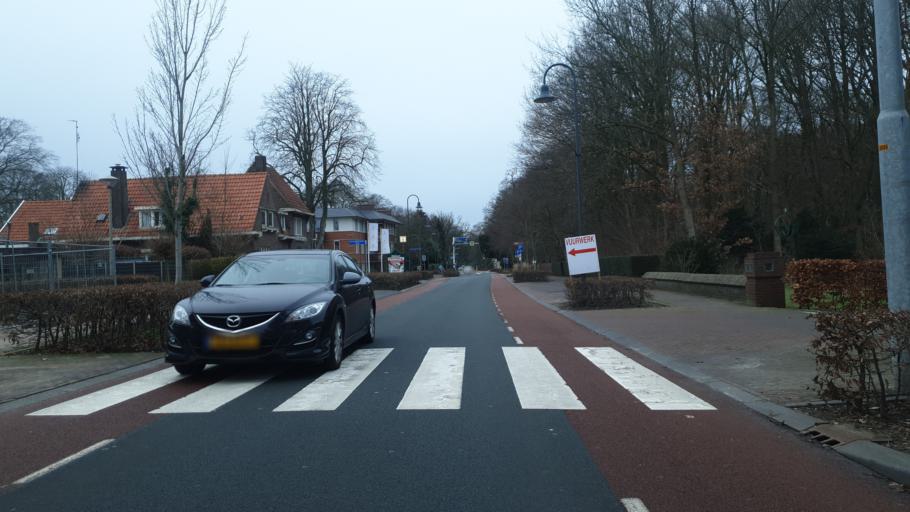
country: NL
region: Gelderland
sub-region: Gemeente Groesbeek
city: Berg en Dal
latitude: 51.8196
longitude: 5.9218
